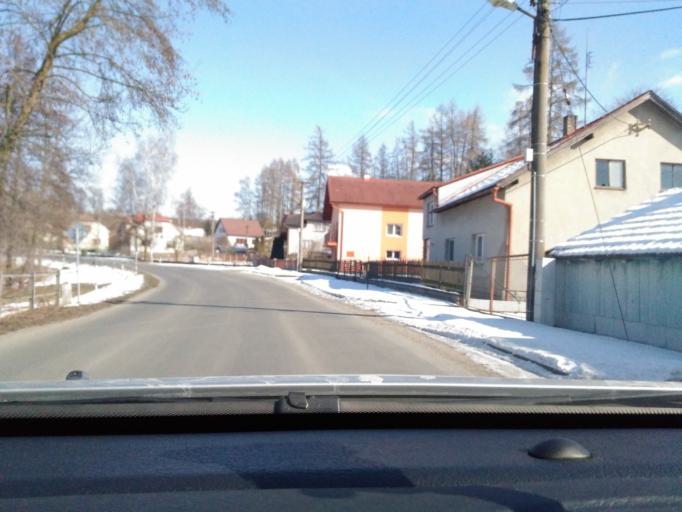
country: CZ
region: Vysocina
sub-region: Okres Zd'ar nad Sazavou
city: Nove Veseli
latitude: 49.4881
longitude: 15.9942
